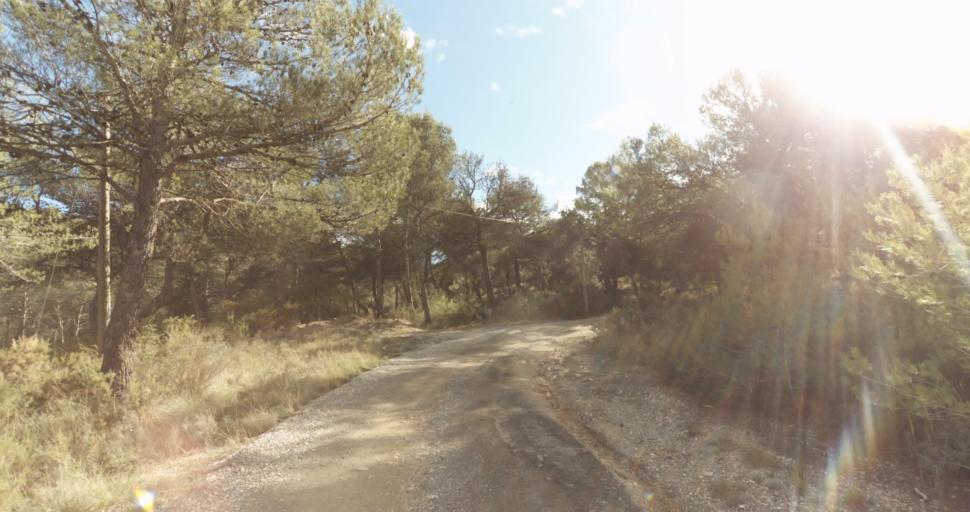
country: FR
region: Provence-Alpes-Cote d'Azur
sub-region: Departement des Bouches-du-Rhone
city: Venelles
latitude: 43.6081
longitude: 5.4990
